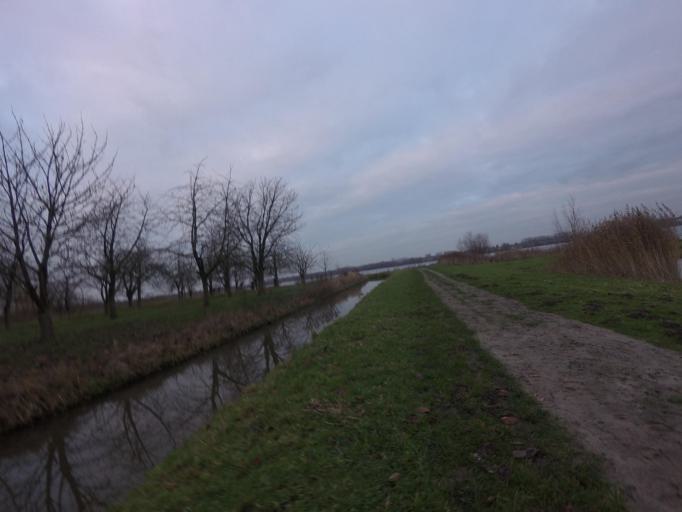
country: NL
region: Utrecht
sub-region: Stichtse Vecht
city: Spechtenkamp
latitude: 52.1196
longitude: 5.0086
